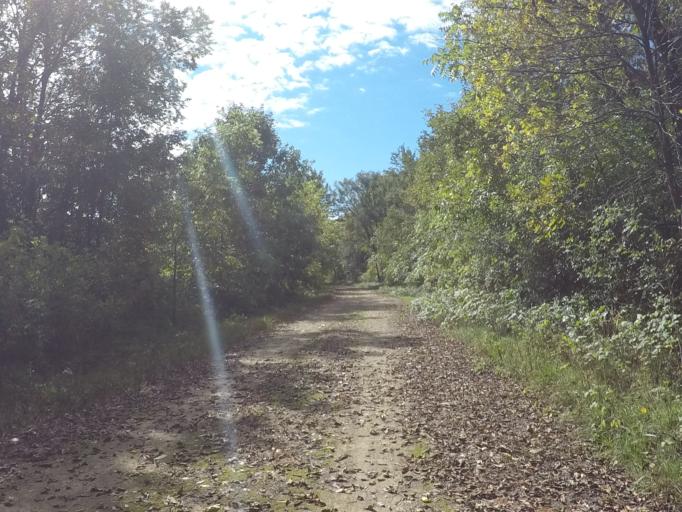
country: US
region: Wisconsin
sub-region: Richland County
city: Richland Center
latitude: 43.2262
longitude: -90.2979
